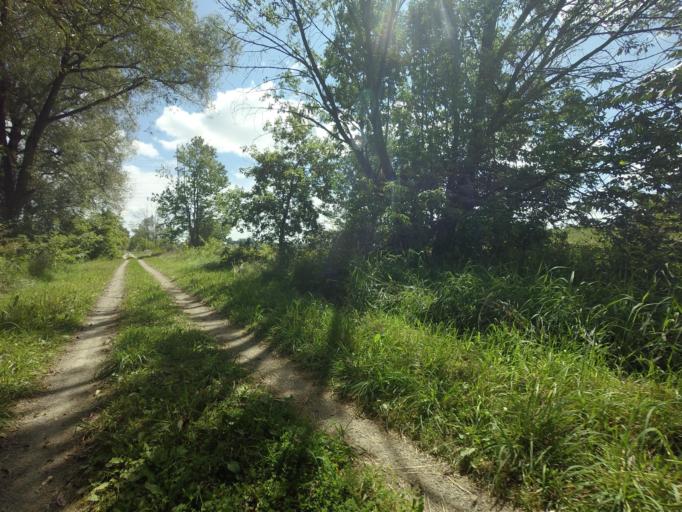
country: CA
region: Ontario
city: Orangeville
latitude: 43.7925
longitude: -80.2681
